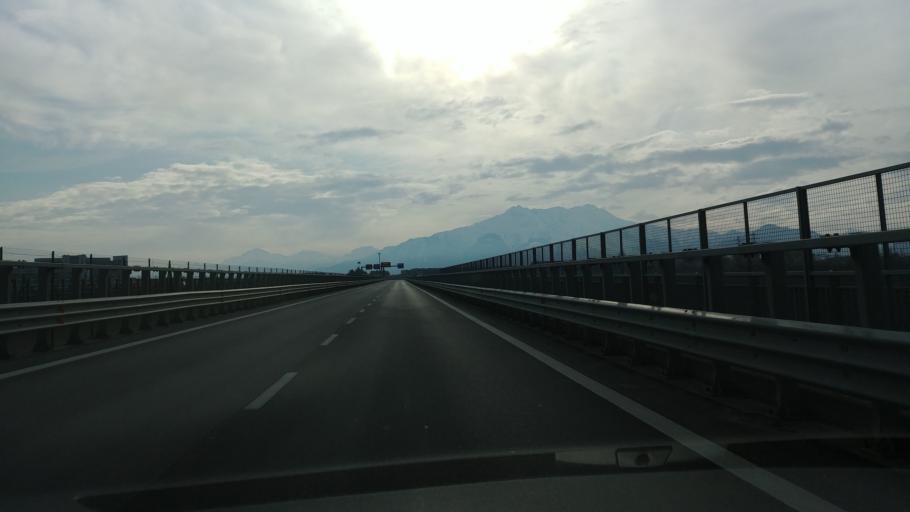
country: IT
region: Piedmont
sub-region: Provincia di Cuneo
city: Cuneo
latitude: 44.3850
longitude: 7.5230
